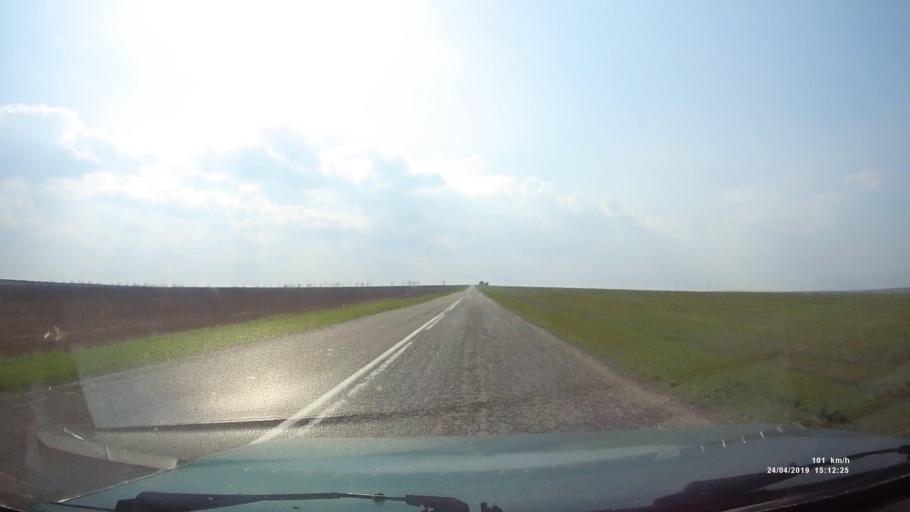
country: RU
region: Rostov
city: Remontnoye
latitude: 46.5464
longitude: 43.3009
